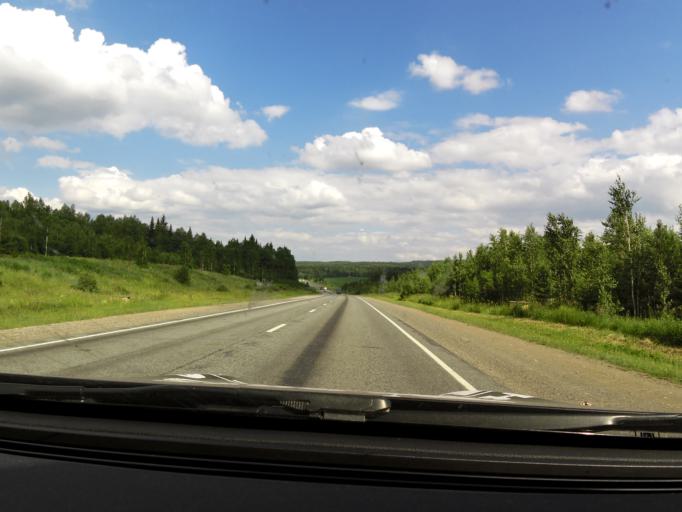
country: RU
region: Sverdlovsk
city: Bisert'
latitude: 56.8263
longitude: 59.1568
